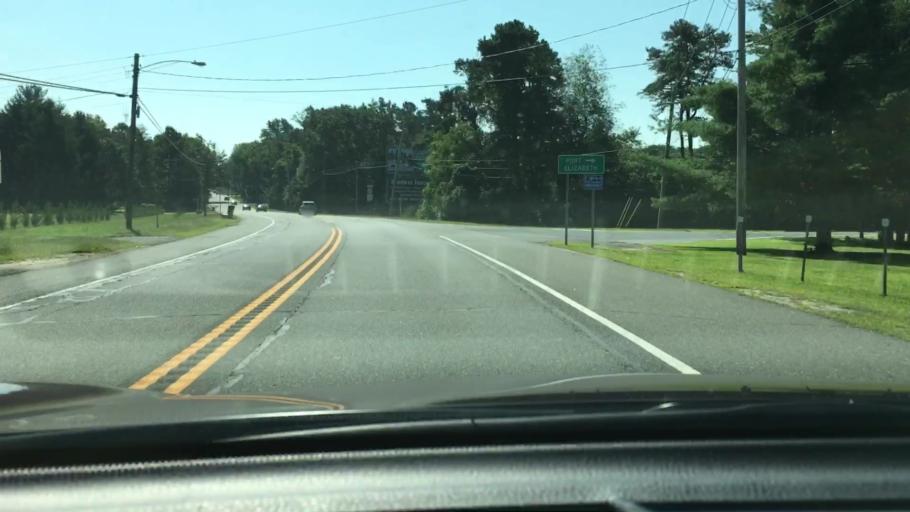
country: US
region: New Jersey
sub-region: Cumberland County
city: Laurel Lake
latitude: 39.3704
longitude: -74.9421
